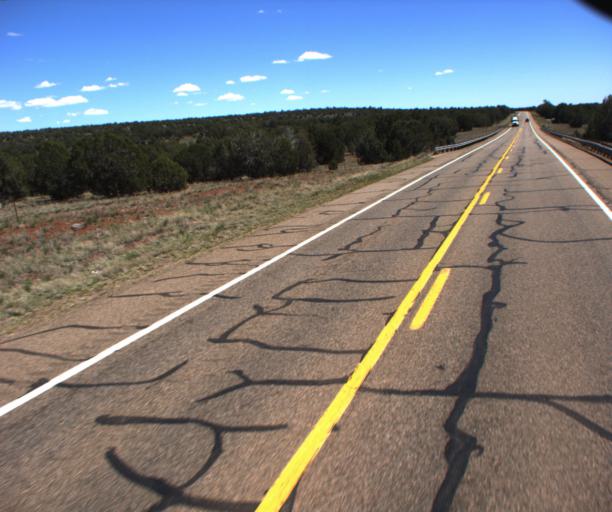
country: US
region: Arizona
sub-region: Yavapai County
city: Paulden
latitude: 35.1162
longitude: -112.4328
